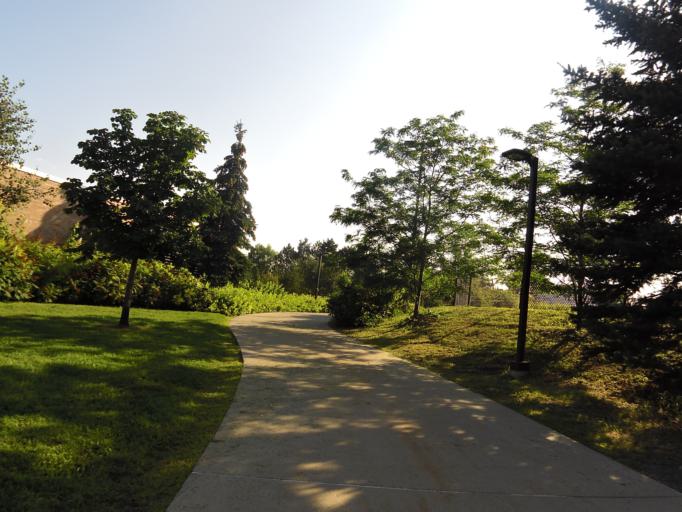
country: CA
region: Ontario
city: Bells Corners
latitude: 45.3355
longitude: -75.8072
